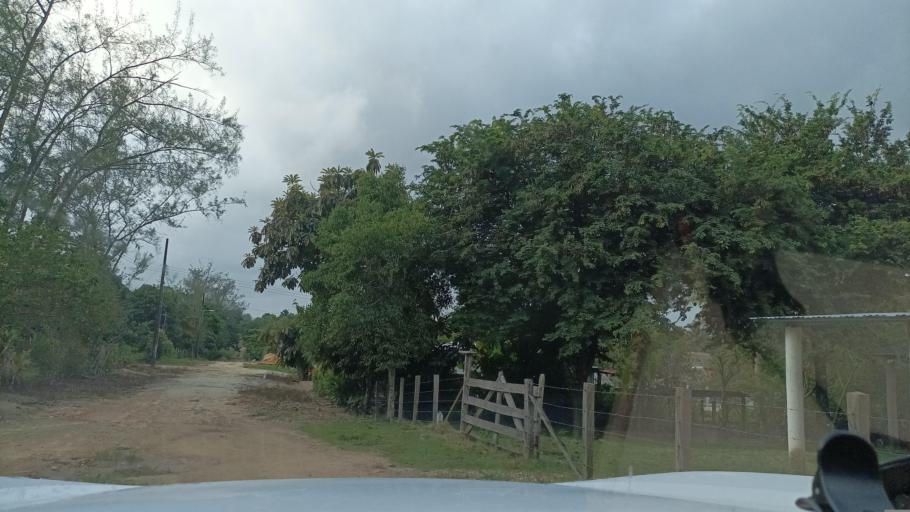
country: MX
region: Veracruz
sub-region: Moloacan
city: Cuichapa
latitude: 17.9237
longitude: -94.3662
